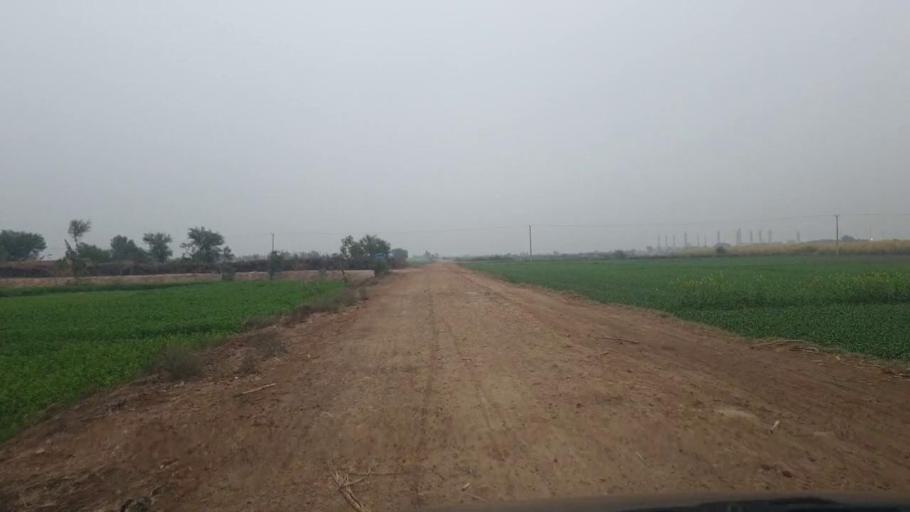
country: PK
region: Sindh
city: Tando Adam
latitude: 25.8028
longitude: 68.6867
